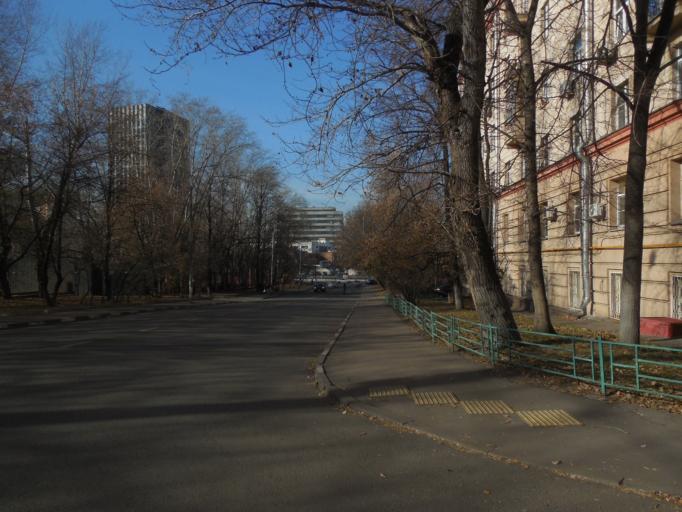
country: RU
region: Moscow
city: Lefortovo
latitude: 55.7766
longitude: 37.7048
